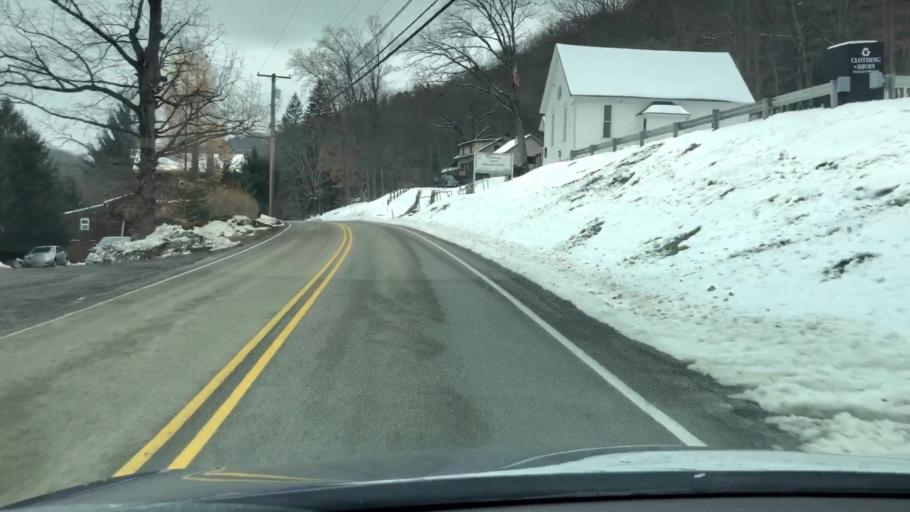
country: US
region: Pennsylvania
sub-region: Elk County
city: Saint Marys
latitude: 41.2848
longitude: -78.4550
